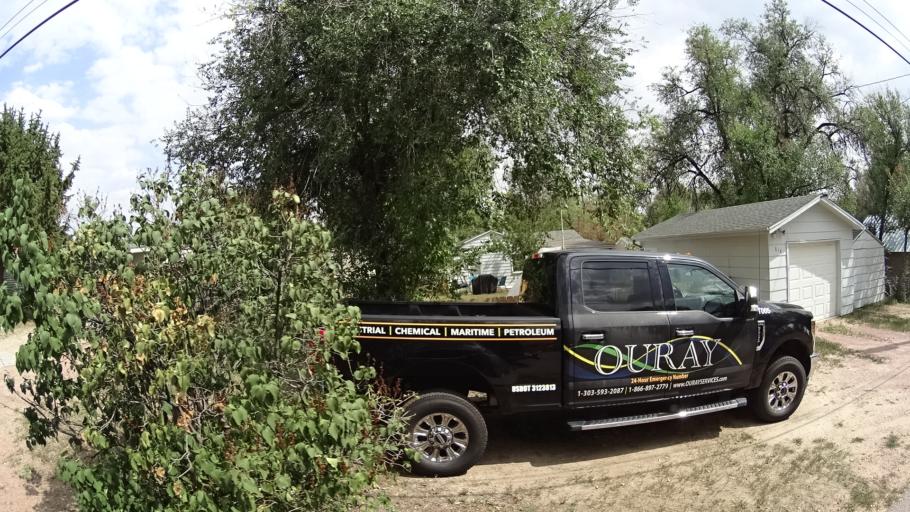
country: US
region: Colorado
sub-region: El Paso County
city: Colorado Springs
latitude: 38.8443
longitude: -104.7894
